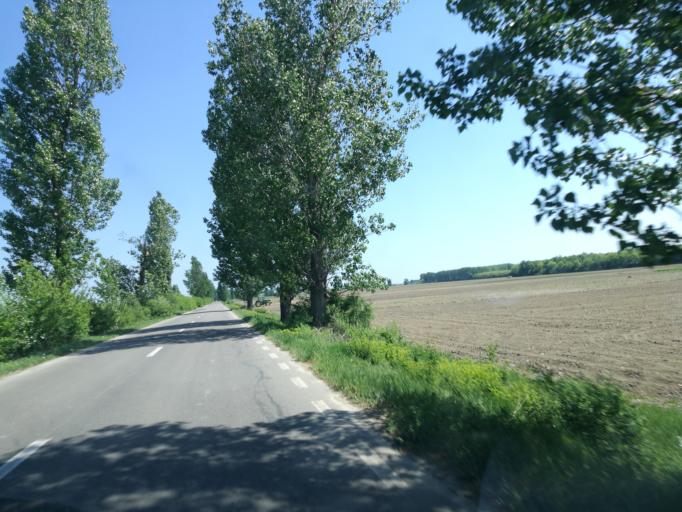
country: RO
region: Ialomita
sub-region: Comuna Adancata
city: Adancata
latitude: 44.7537
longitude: 26.4278
